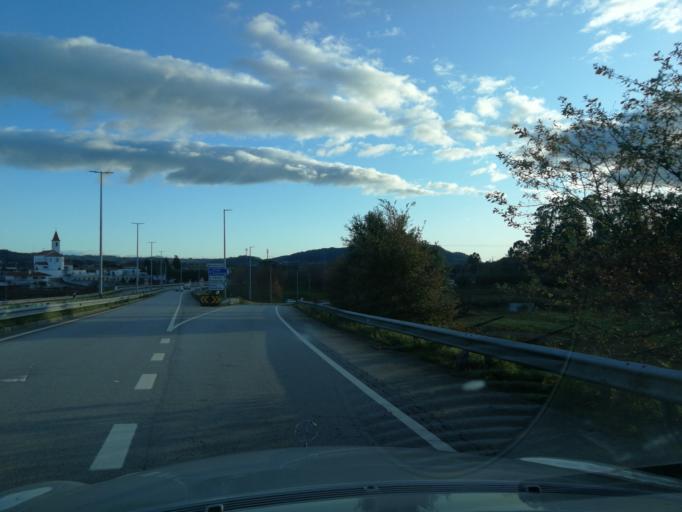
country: PT
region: Braga
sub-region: Barcelos
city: Vila Frescainha
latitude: 41.5365
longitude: -8.6387
